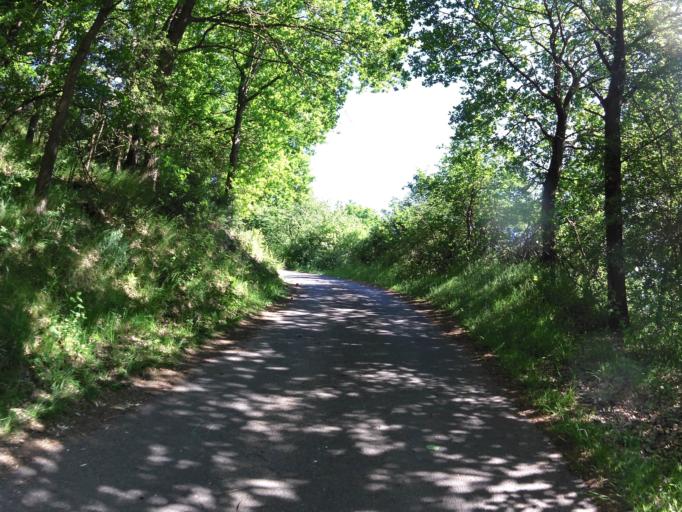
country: DE
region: Thuringia
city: Unterbreizbach
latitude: 50.8284
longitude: 9.9948
